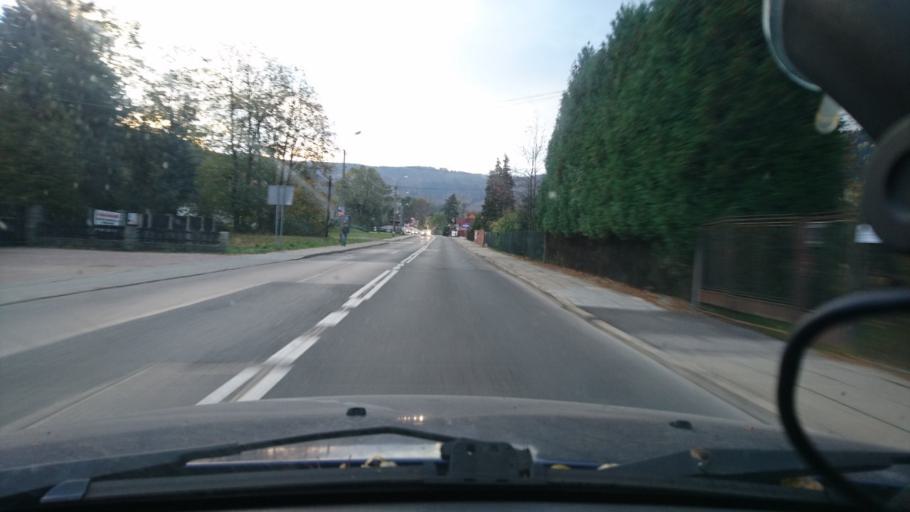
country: PL
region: Silesian Voivodeship
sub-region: Powiat bielski
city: Wilkowice
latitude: 49.7992
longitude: 19.0907
